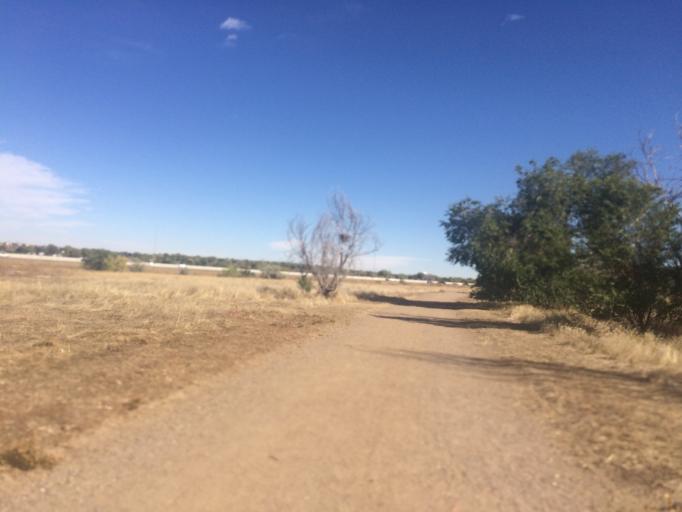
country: US
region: Colorado
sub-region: Broomfield County
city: Broomfield
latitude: 39.8790
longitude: -105.0700
